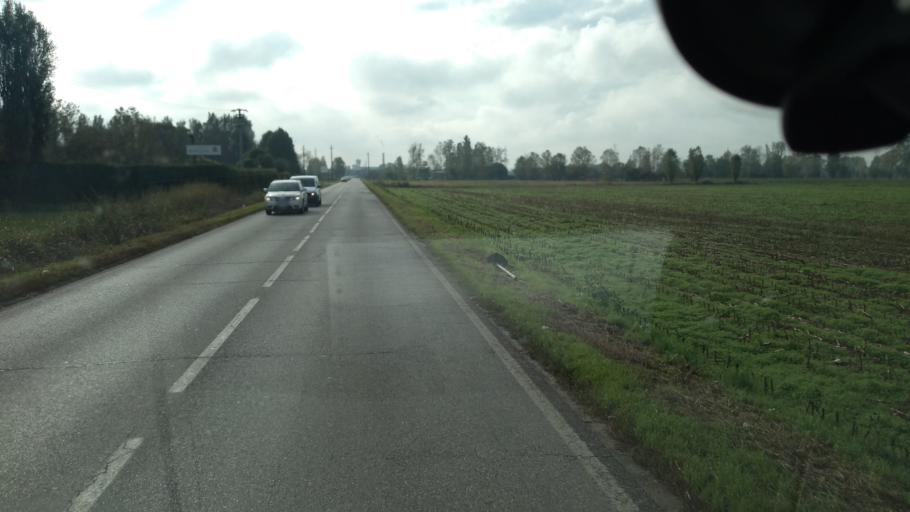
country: IT
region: Lombardy
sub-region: Provincia di Bergamo
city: Vidalengo
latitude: 45.5320
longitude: 9.6389
